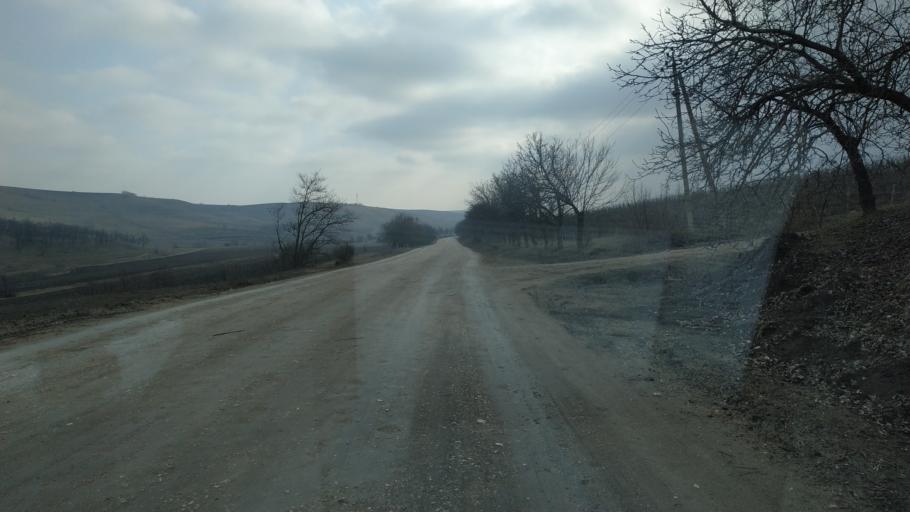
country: MD
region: Hincesti
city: Dancu
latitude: 46.9213
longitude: 28.3284
